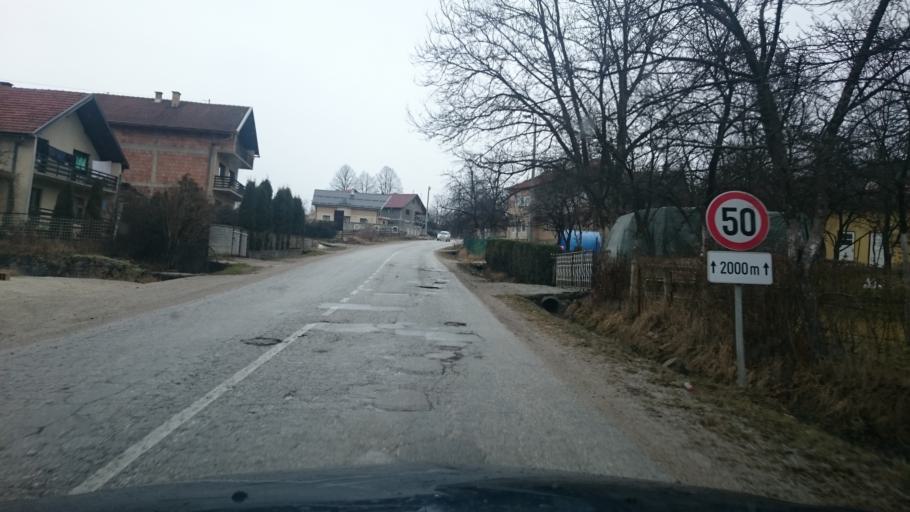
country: BA
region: Federation of Bosnia and Herzegovina
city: Turbe
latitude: 44.2429
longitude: 17.5844
